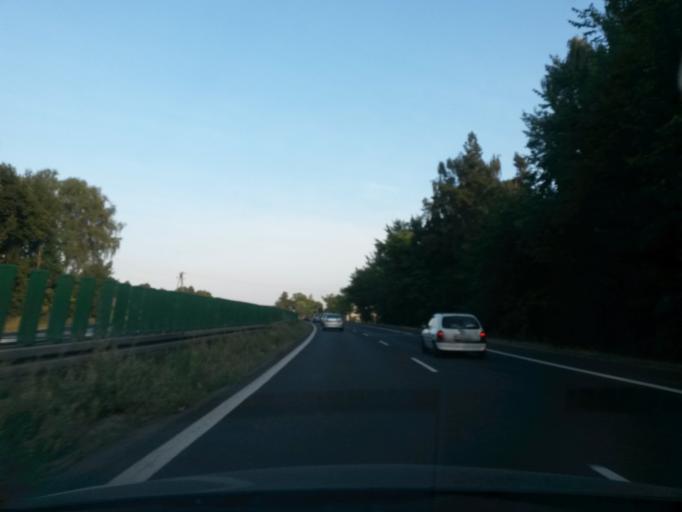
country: PL
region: Masovian Voivodeship
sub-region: Powiat nowodworski
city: Zakroczym
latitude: 52.4537
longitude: 20.5830
